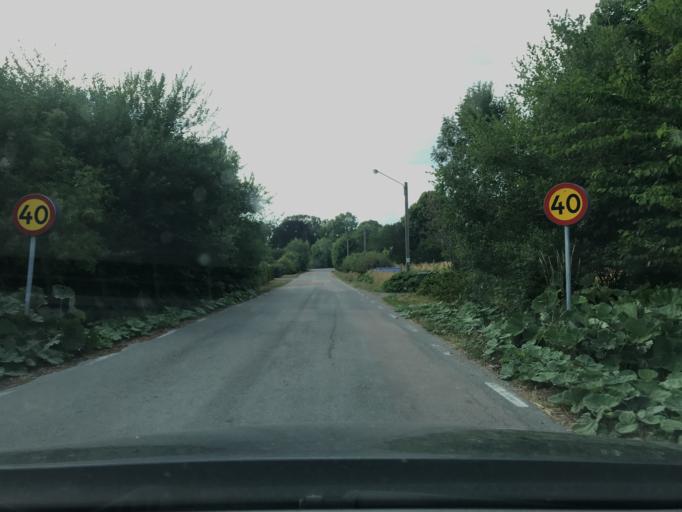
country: SE
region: Skane
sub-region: Simrishamns Kommun
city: Kivik
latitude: 55.5245
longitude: 14.1672
